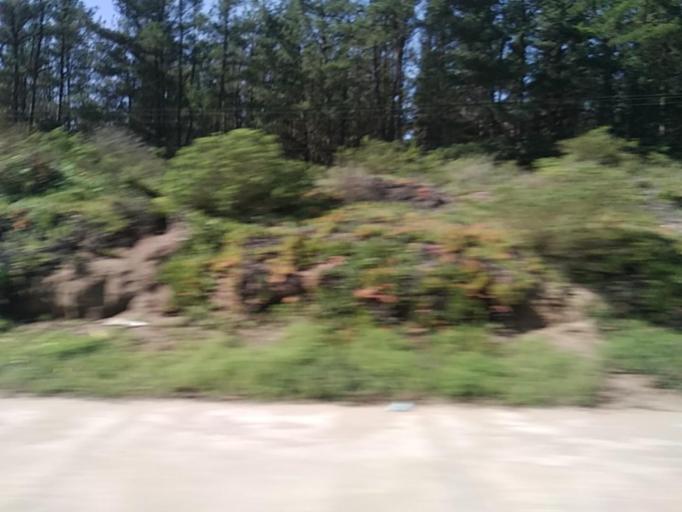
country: CL
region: Valparaiso
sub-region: Provincia de Valparaiso
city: Vina del Mar
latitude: -32.9560
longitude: -71.5391
